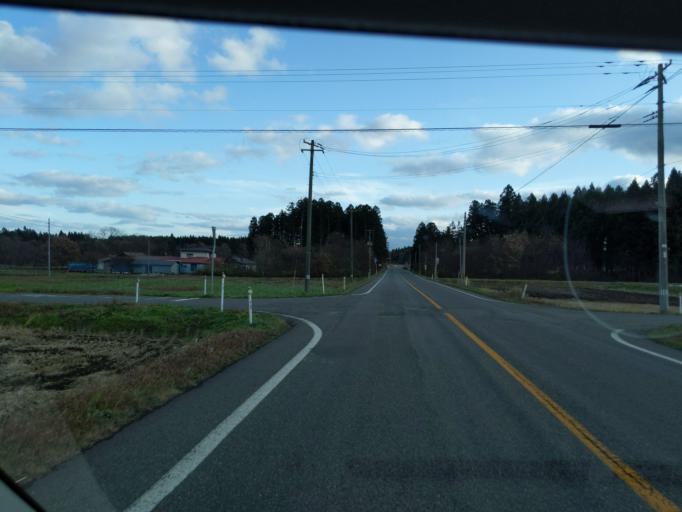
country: JP
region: Iwate
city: Mizusawa
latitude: 39.1644
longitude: 141.0492
